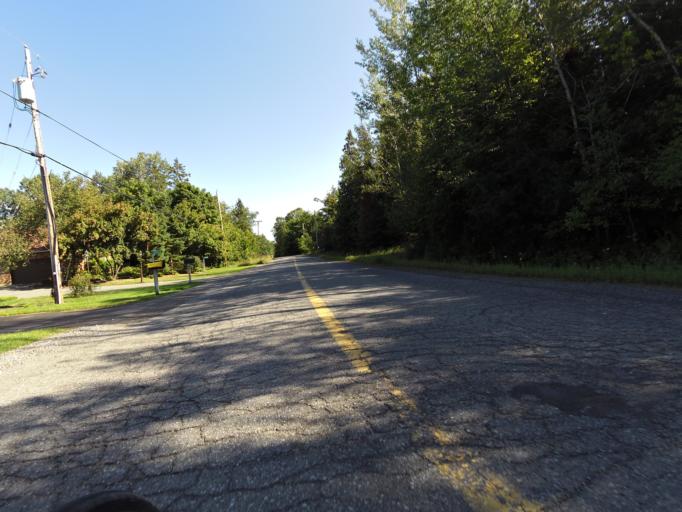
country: CA
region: Ontario
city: Bells Corners
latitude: 45.4649
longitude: -75.9753
